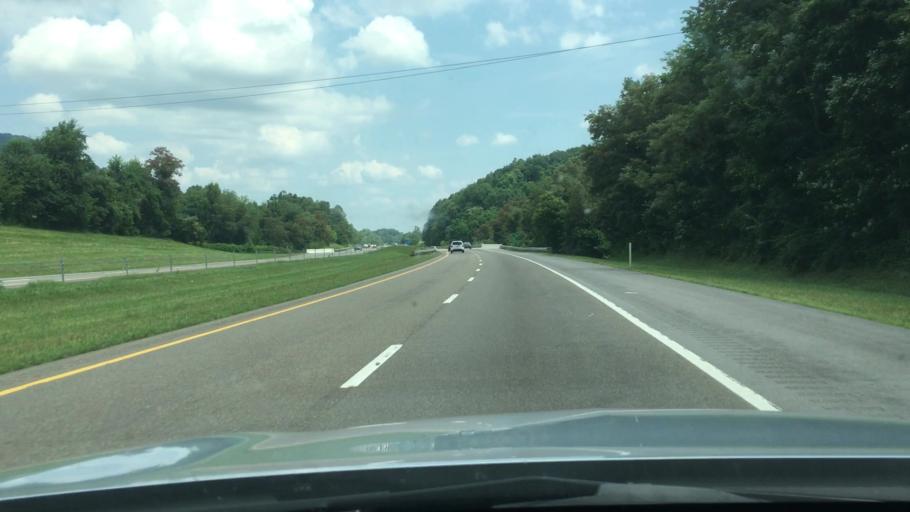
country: US
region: Tennessee
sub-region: Unicoi County
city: Unicoi
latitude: 36.2396
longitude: -82.3276
